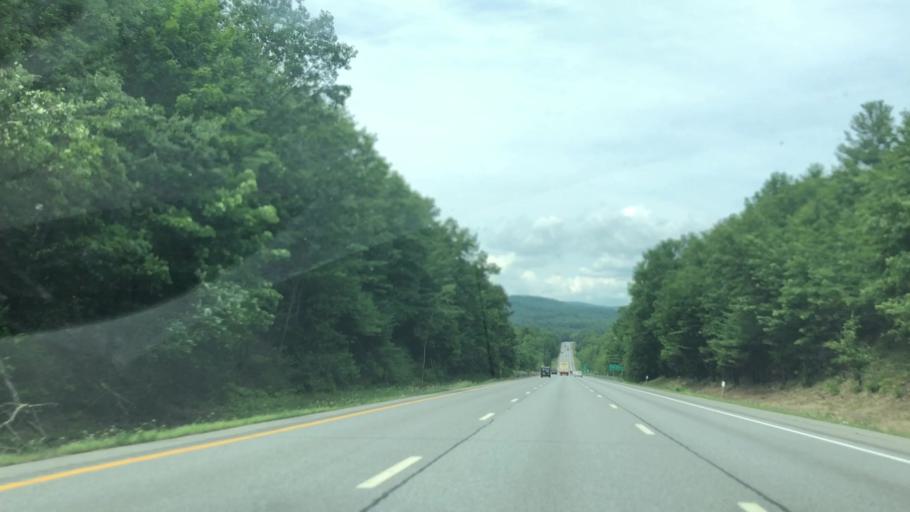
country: US
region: New York
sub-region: Warren County
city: Glens Falls North
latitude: 43.3443
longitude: -73.6916
